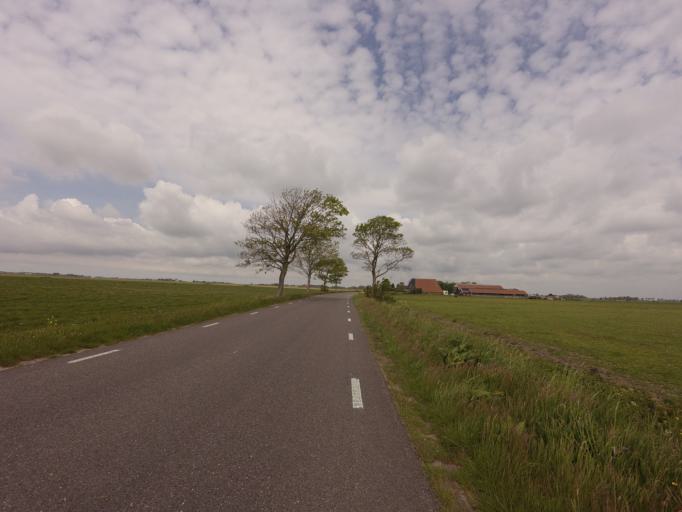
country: NL
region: Friesland
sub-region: Sudwest Fryslan
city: Bolsward
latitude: 53.0963
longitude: 5.5345
